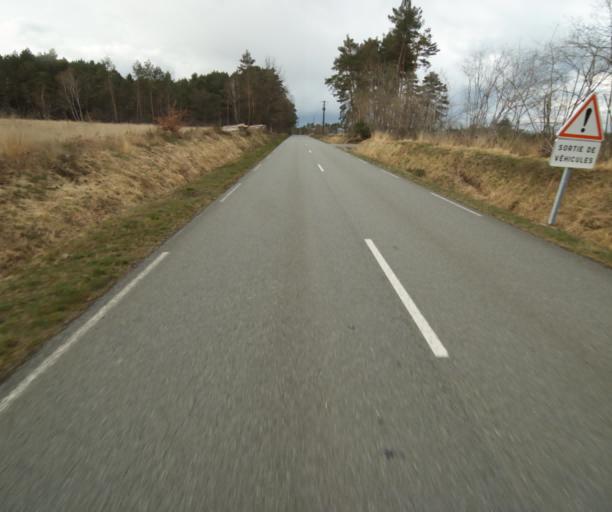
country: FR
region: Limousin
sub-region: Departement de la Correze
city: Saint-Privat
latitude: 45.2053
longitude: 2.0044
